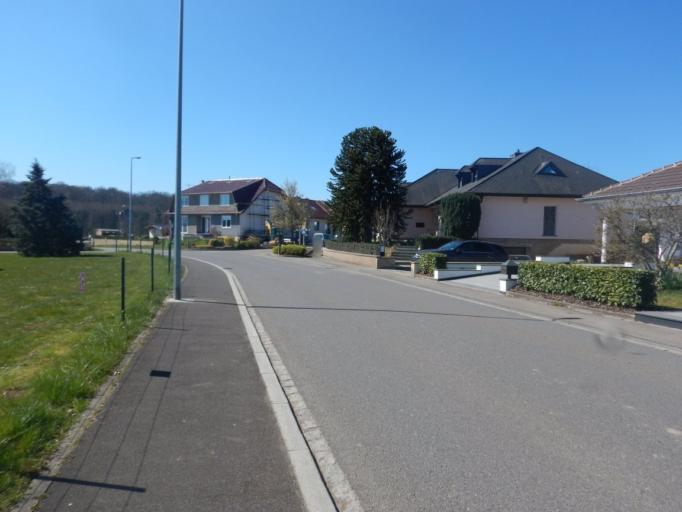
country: LU
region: Luxembourg
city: Schouweiler
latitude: 49.5972
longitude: 5.9455
